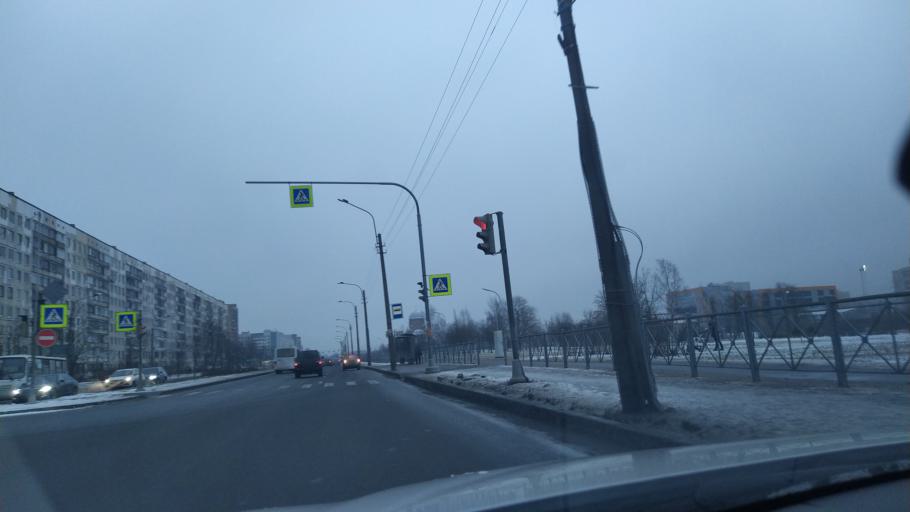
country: RU
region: St.-Petersburg
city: Grazhdanka
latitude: 60.0276
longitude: 30.4033
